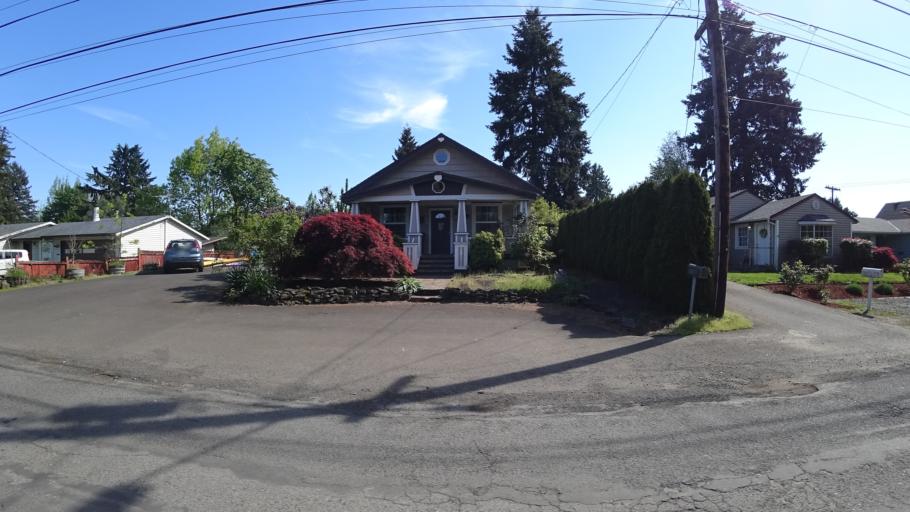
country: US
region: Oregon
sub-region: Clackamas County
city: Milwaukie
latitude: 45.4481
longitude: -122.6239
